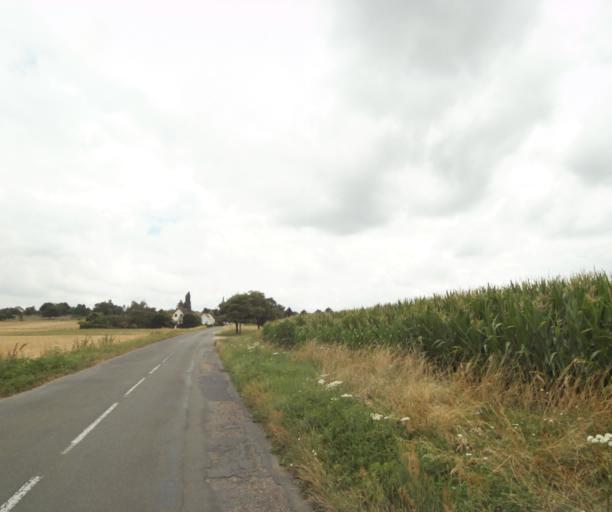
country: FR
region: Centre
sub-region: Departement du Loiret
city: Mardie
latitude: 47.8818
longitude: 2.0524
